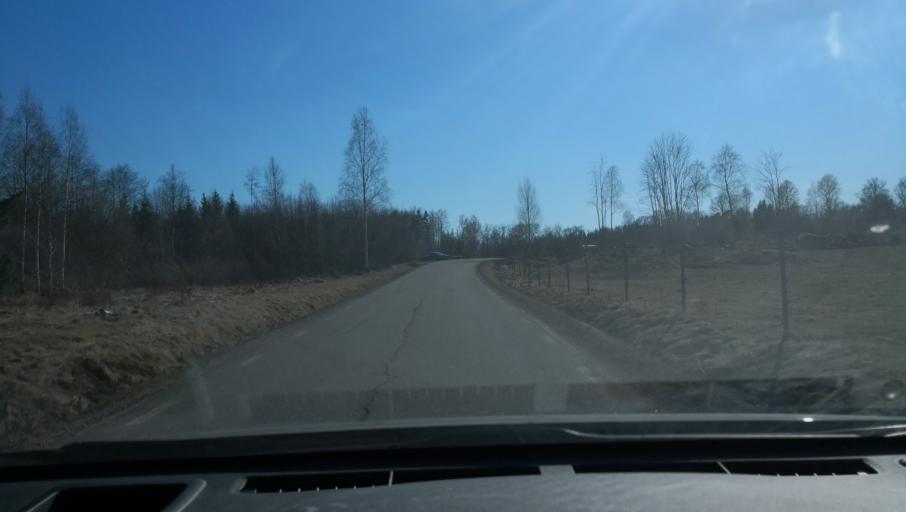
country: SE
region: Dalarna
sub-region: Avesta Kommun
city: Avesta
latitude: 60.0726
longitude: 16.3775
